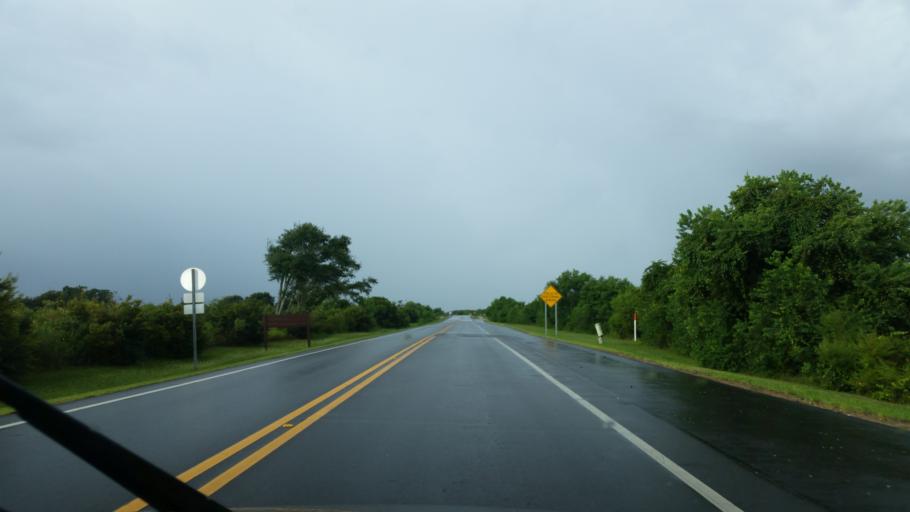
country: US
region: Alabama
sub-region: Baldwin County
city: Gulf Shores
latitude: 30.2585
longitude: -87.6523
